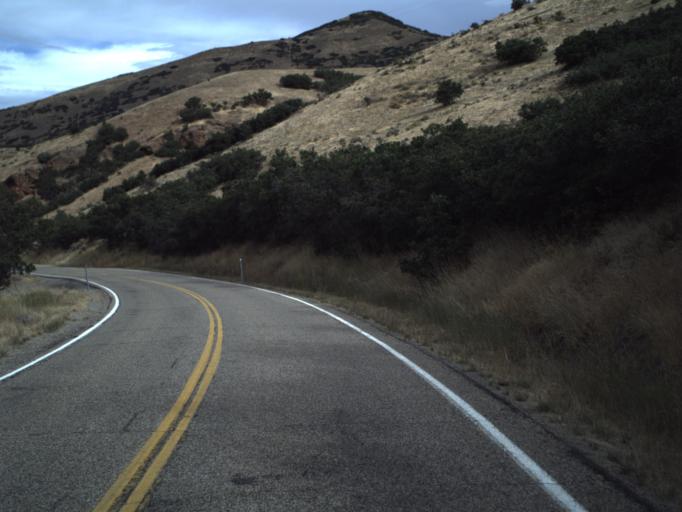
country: US
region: Utah
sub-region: Morgan County
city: Morgan
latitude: 40.9223
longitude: -111.6028
